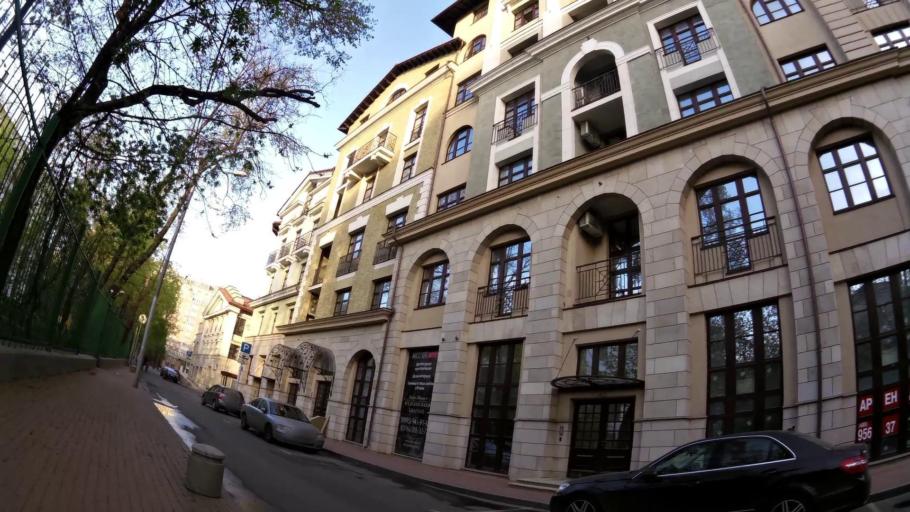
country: RU
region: Moscow
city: Moscow
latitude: 55.7755
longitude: 37.6001
